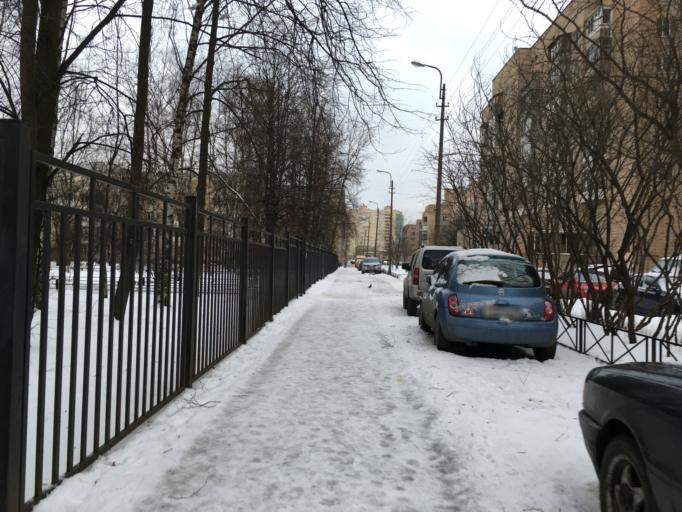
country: RU
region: St.-Petersburg
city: Kupchino
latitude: 59.8614
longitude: 30.3127
